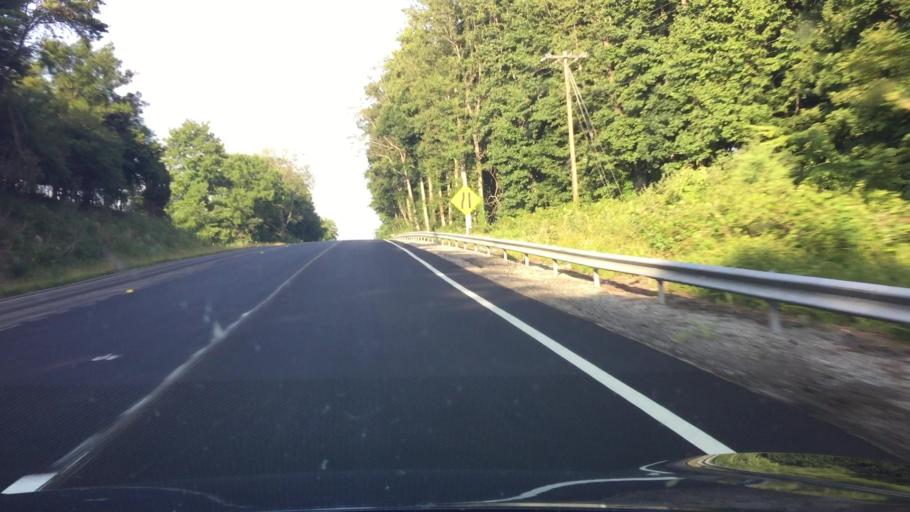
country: US
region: Virginia
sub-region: Montgomery County
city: Christiansburg
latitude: 37.1313
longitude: -80.4746
